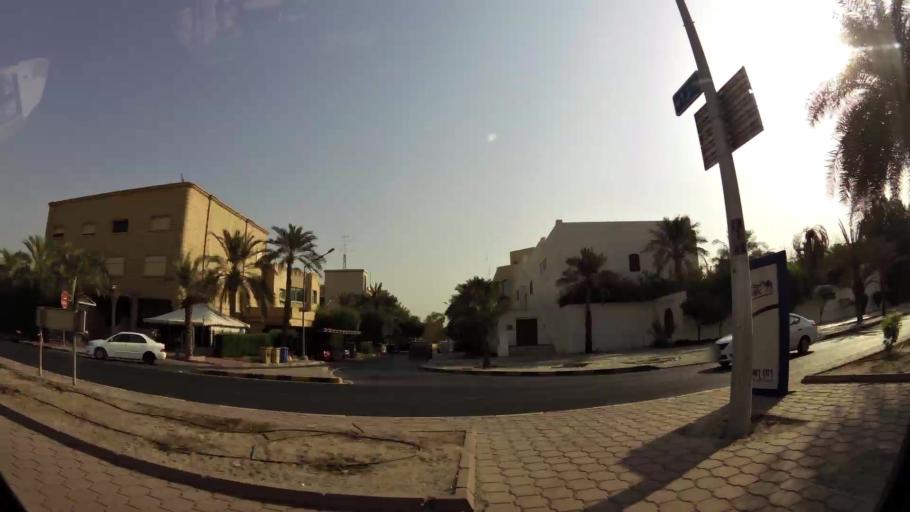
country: KW
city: Bayan
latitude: 29.3119
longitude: 48.0410
